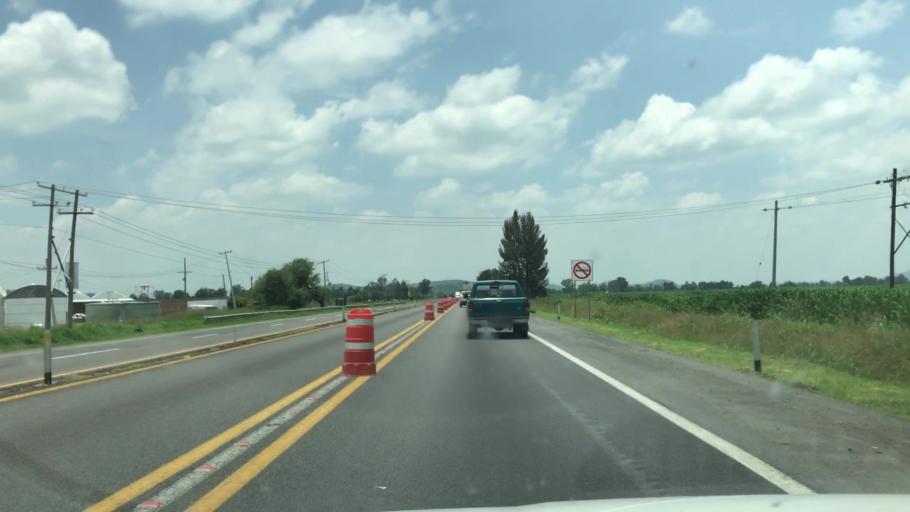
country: MX
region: Guanajuato
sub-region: Irapuato
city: San Ignacio de Rivera (Ojo de Agua)
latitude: 20.5110
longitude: -101.4705
